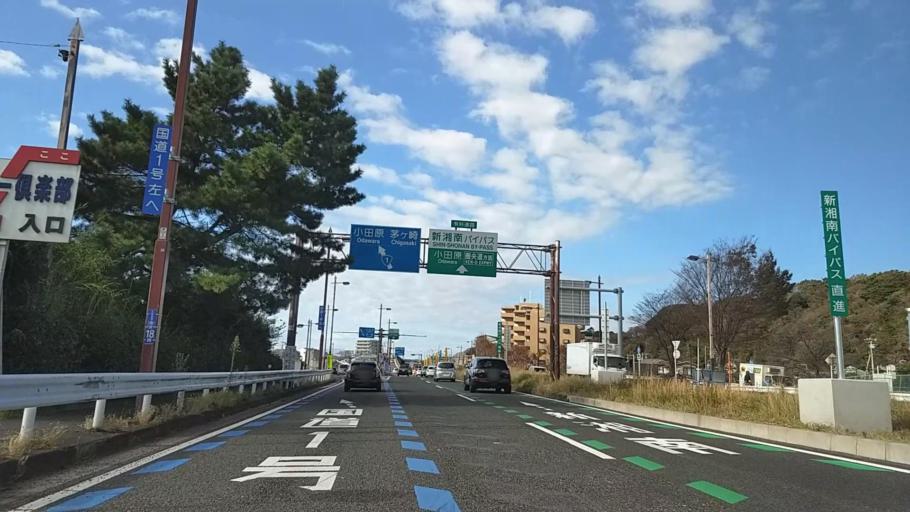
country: JP
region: Kanagawa
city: Fujisawa
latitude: 35.3482
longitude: 139.4537
